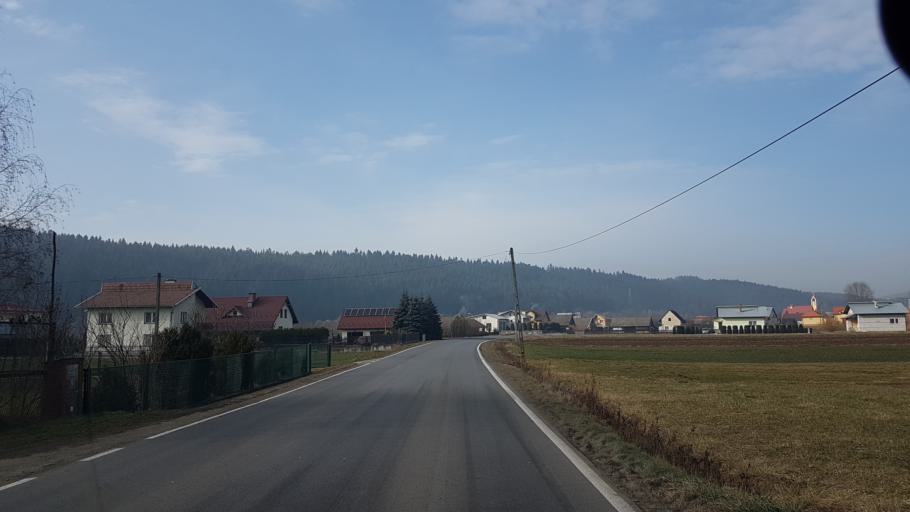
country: PL
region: Lesser Poland Voivodeship
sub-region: Powiat nowosadecki
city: Podegrodzie
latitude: 49.5610
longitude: 20.5614
